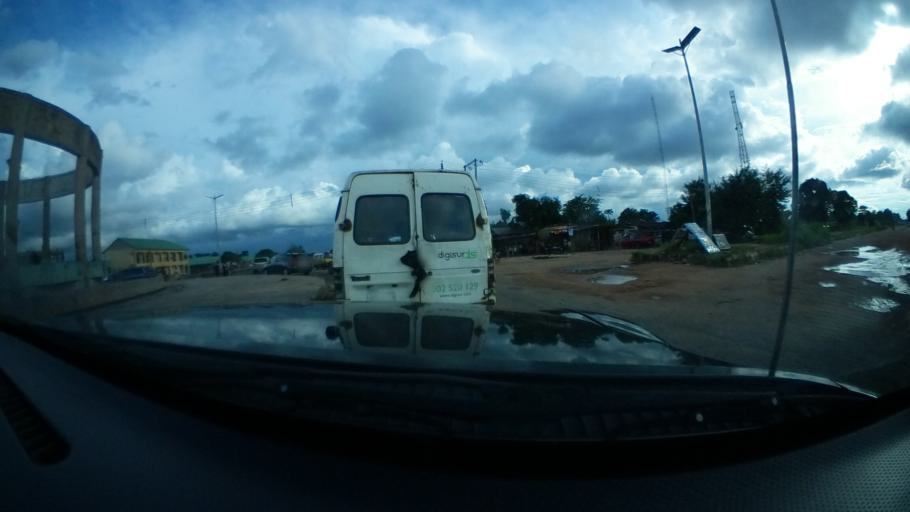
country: NG
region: Imo
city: Orodo
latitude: 5.5880
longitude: 7.0160
